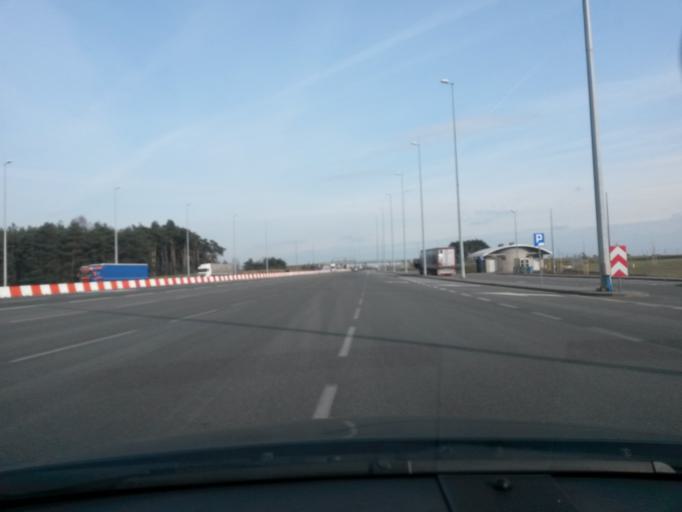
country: PL
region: Greater Poland Voivodeship
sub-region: Powiat slupecki
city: Ladek
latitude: 52.2214
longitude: 17.9520
